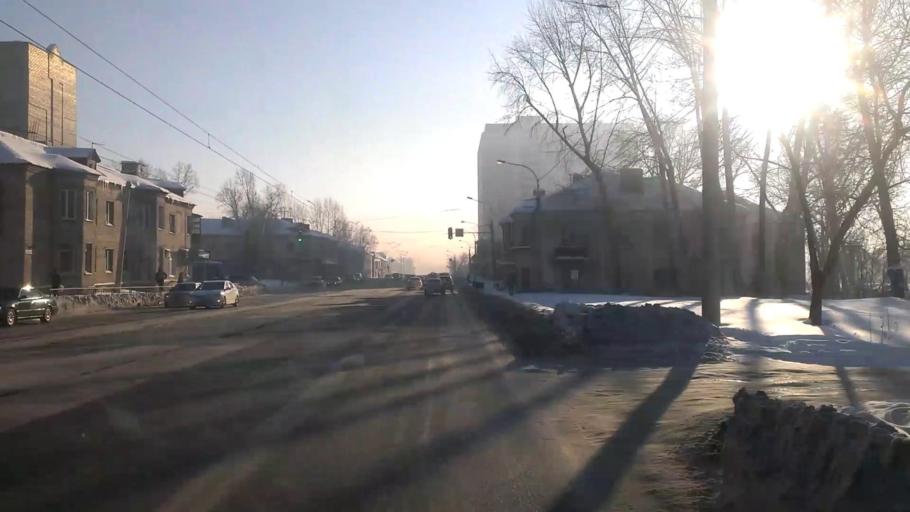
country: RU
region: Altai Krai
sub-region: Gorod Barnaulskiy
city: Barnaul
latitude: 53.3476
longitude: 83.7306
